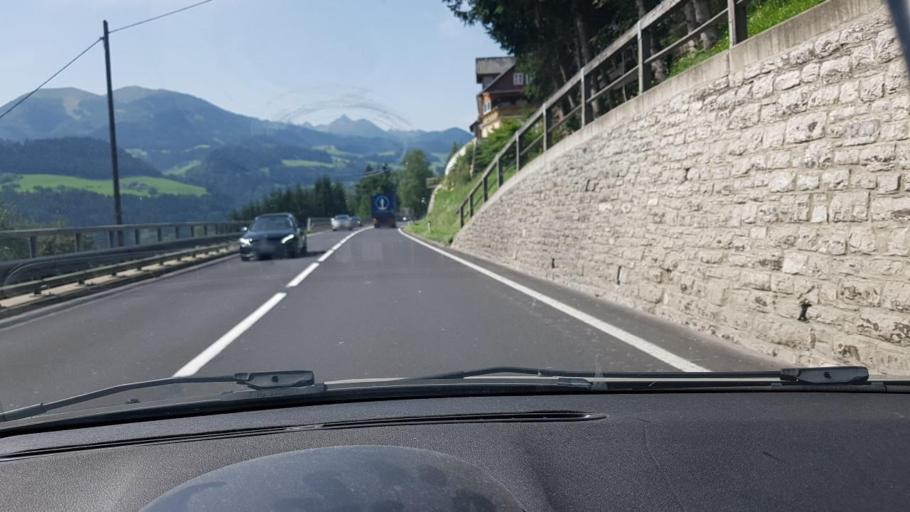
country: AT
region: Styria
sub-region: Politischer Bezirk Liezen
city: Grobming
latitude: 47.4348
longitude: 13.8998
